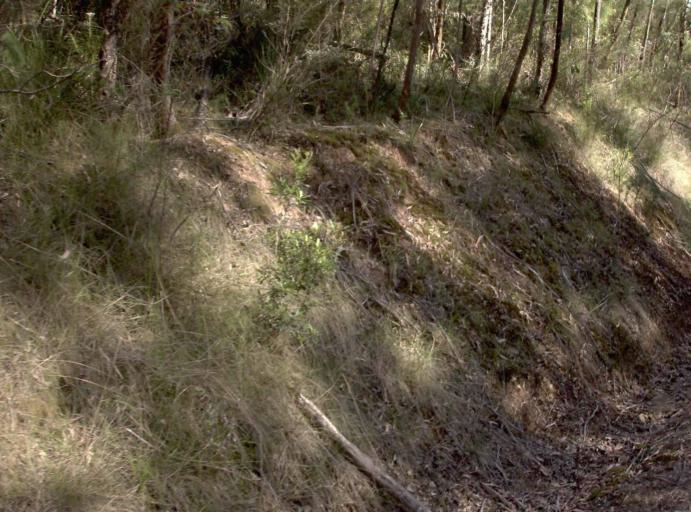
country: AU
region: Victoria
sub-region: East Gippsland
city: Lakes Entrance
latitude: -37.4859
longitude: 148.5538
